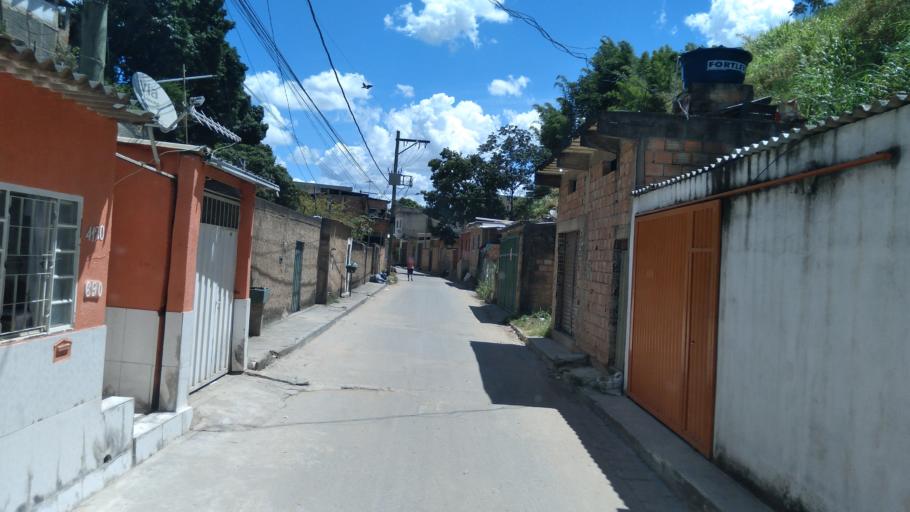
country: BR
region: Minas Gerais
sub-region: Santa Luzia
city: Santa Luzia
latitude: -19.8391
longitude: -43.8973
